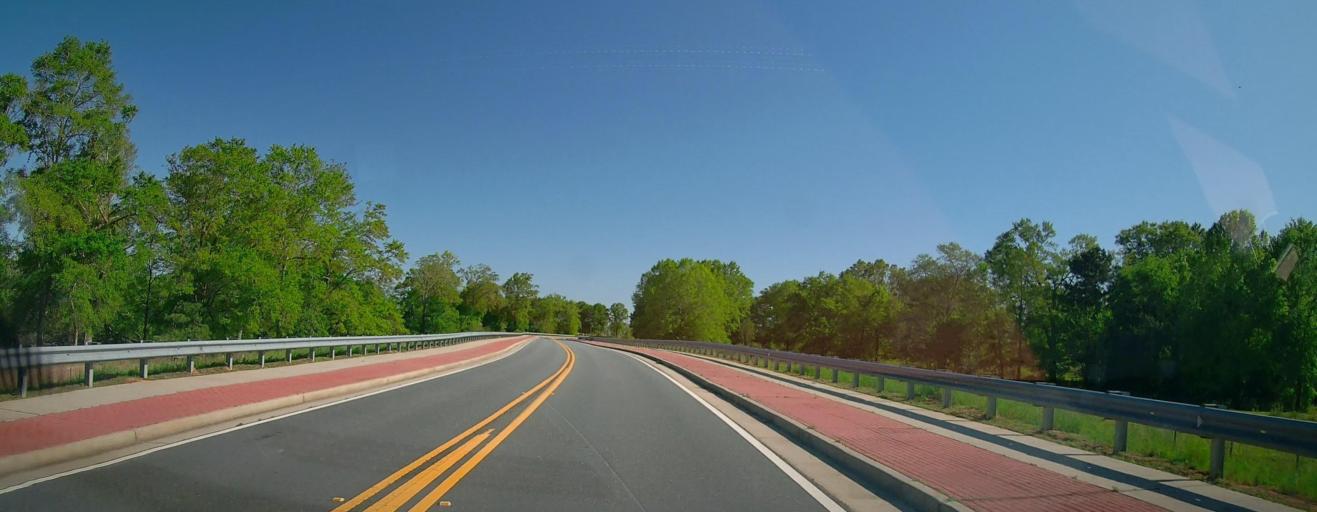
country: US
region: Georgia
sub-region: Houston County
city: Robins Air Force Base
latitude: 32.5500
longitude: -83.5856
